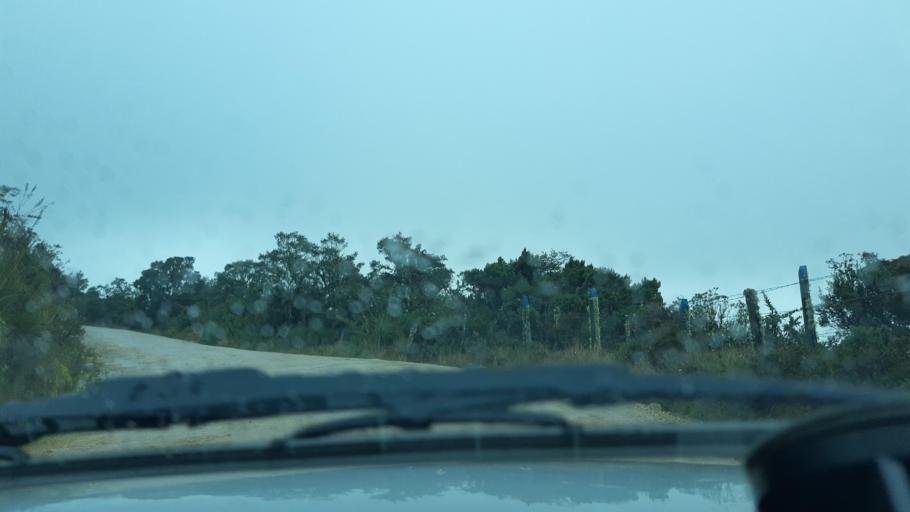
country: CO
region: Cundinamarca
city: Villapinzon
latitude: 5.2183
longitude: -73.5280
